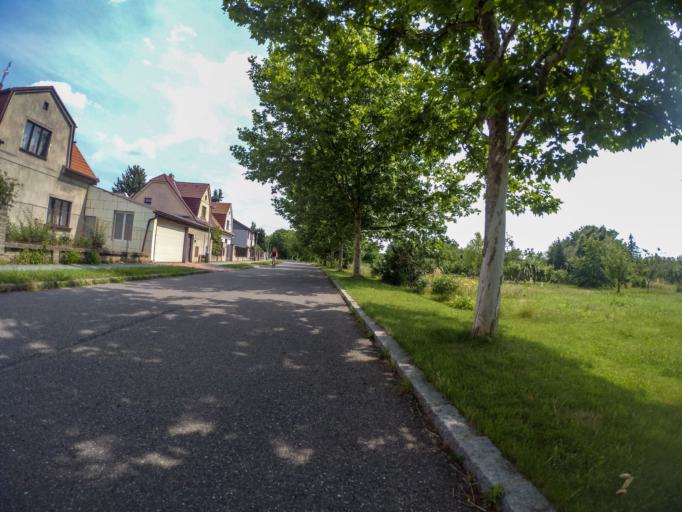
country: CZ
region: Praha
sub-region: Praha 19
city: Kbely
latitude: 50.1291
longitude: 14.5556
